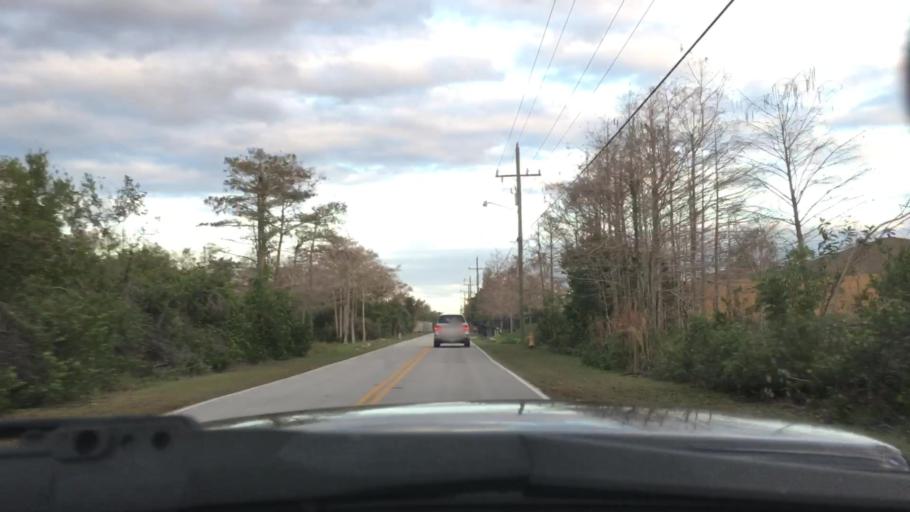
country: US
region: Florida
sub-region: Miami-Dade County
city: Kendall West
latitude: 25.7607
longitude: -80.8383
